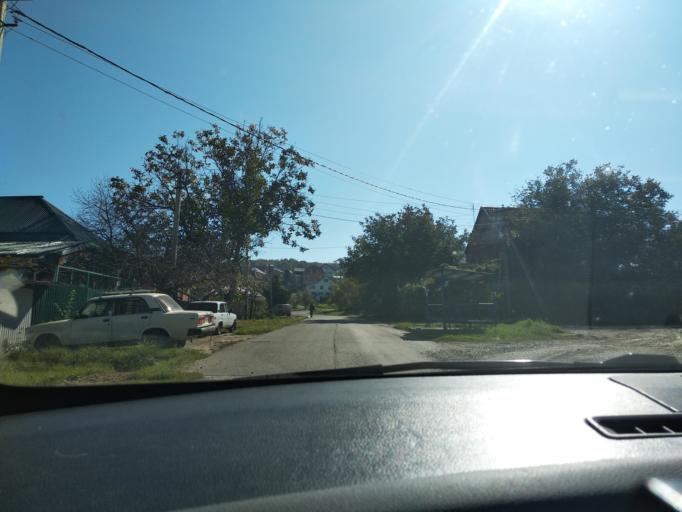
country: RU
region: Krasnodarskiy
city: Goryachiy Klyuch
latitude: 44.6297
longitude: 39.1561
